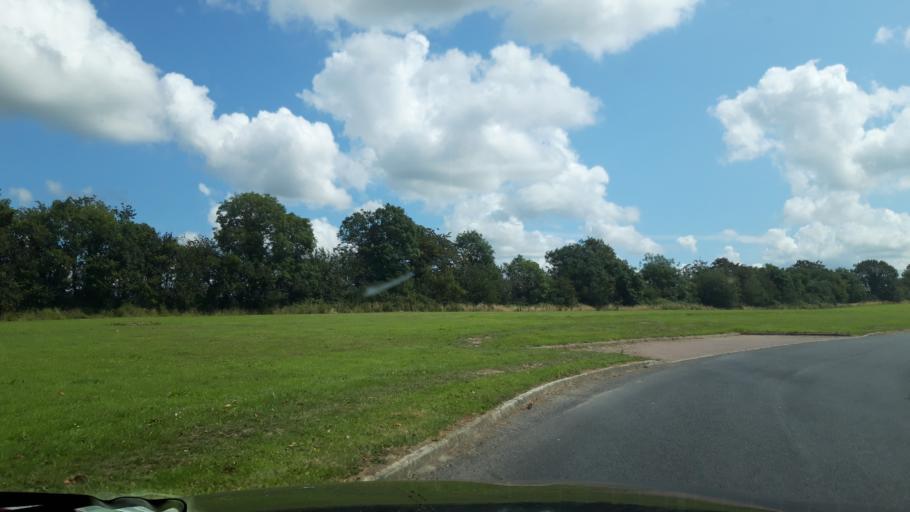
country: IE
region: Munster
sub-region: Waterford
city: Waterford
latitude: 52.2680
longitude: -7.0922
